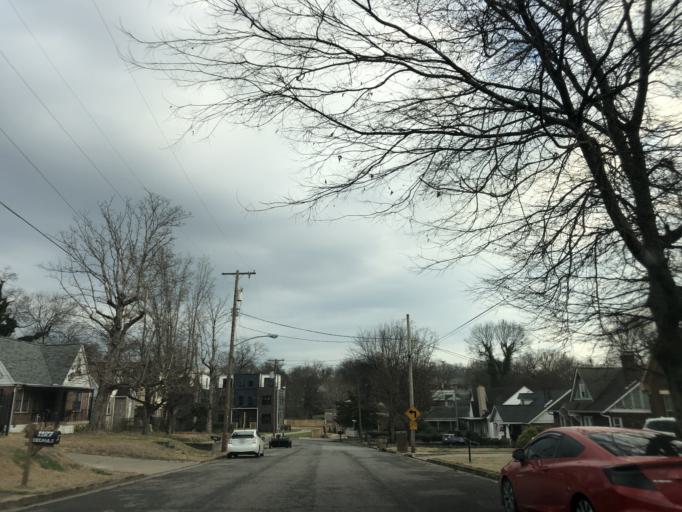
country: US
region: Tennessee
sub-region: Davidson County
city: Nashville
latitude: 36.1988
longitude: -86.7384
